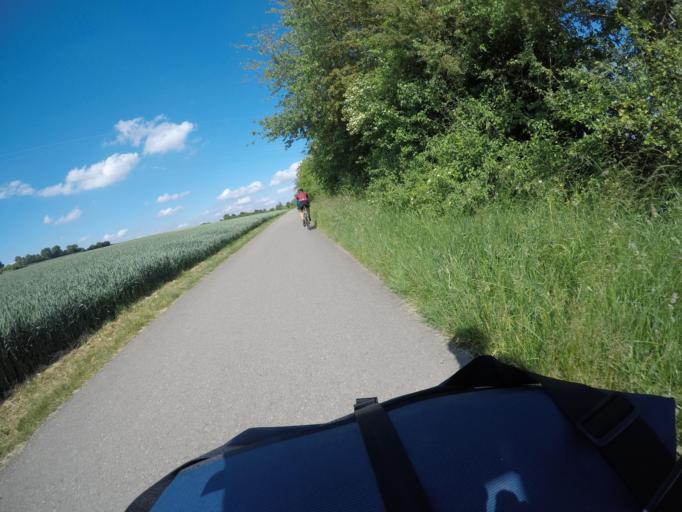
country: DE
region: Baden-Wuerttemberg
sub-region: Regierungsbezirk Stuttgart
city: Gartringen
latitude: 48.6484
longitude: 8.9188
